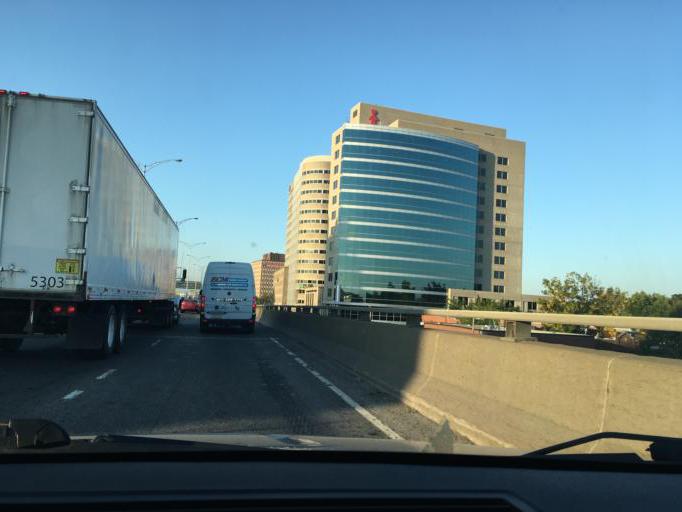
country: CA
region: Quebec
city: Mont-Royal
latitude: 45.5478
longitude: -73.6369
